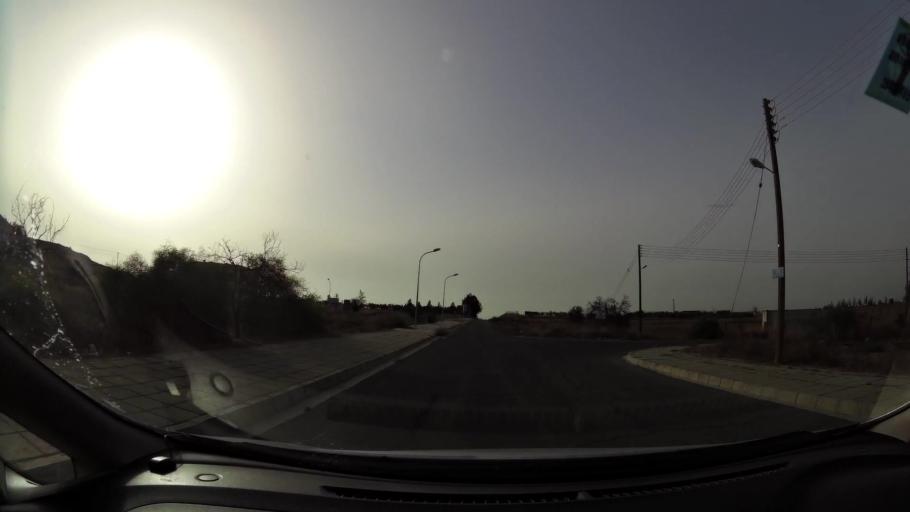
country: CY
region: Lefkosia
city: Dali
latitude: 35.0619
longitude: 33.3864
